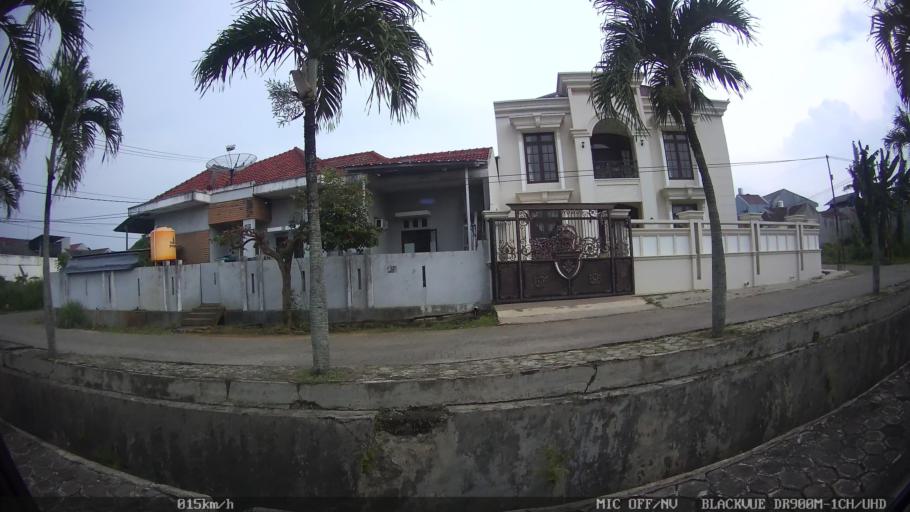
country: ID
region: Lampung
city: Bandarlampung
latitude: -5.4136
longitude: 105.2897
